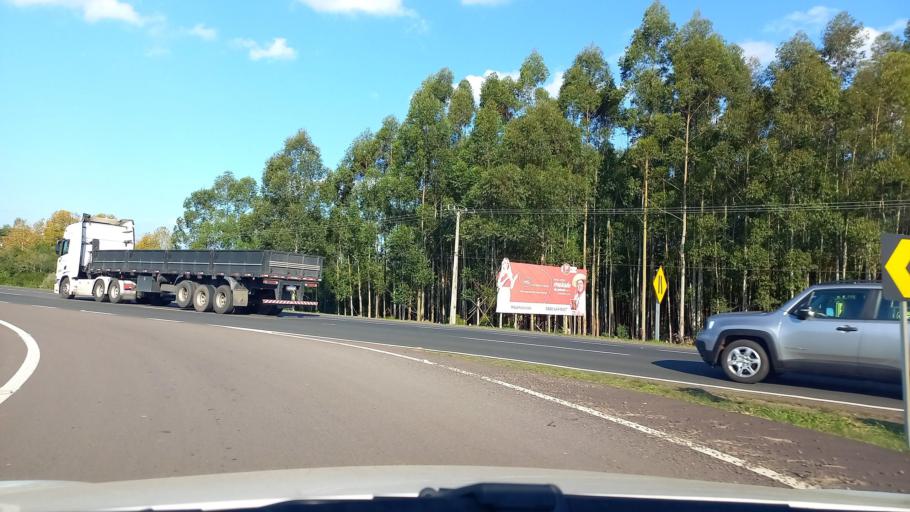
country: BR
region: Rio Grande do Sul
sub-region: Taquari
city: Taquari
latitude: -29.6912
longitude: -51.7105
